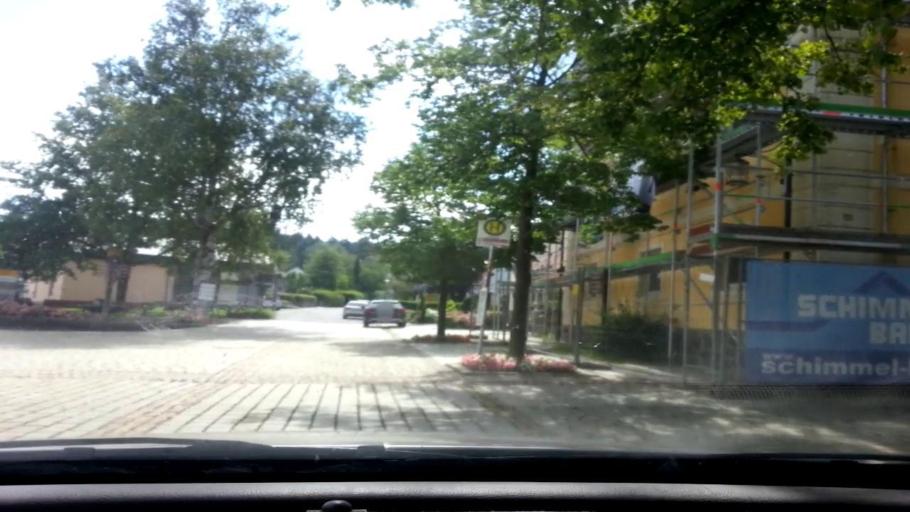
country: DE
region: Bavaria
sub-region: Upper Franconia
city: Bischofsgrun
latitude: 50.0514
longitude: 11.7982
